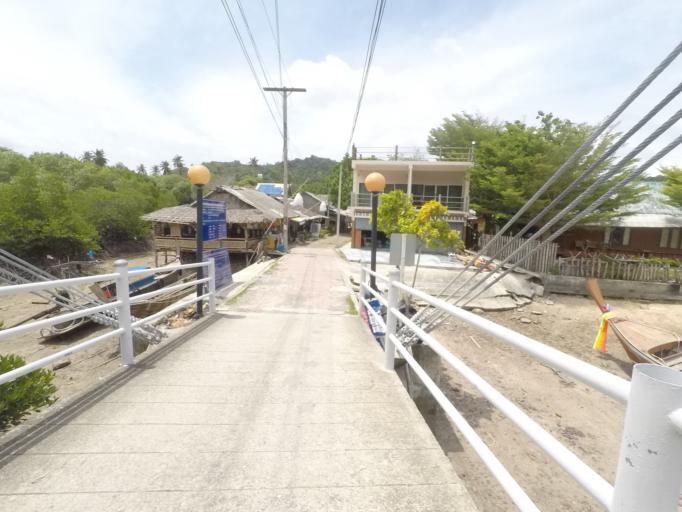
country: TH
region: Phangnga
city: Ban Phru Nai
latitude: 7.7623
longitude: 98.7699
